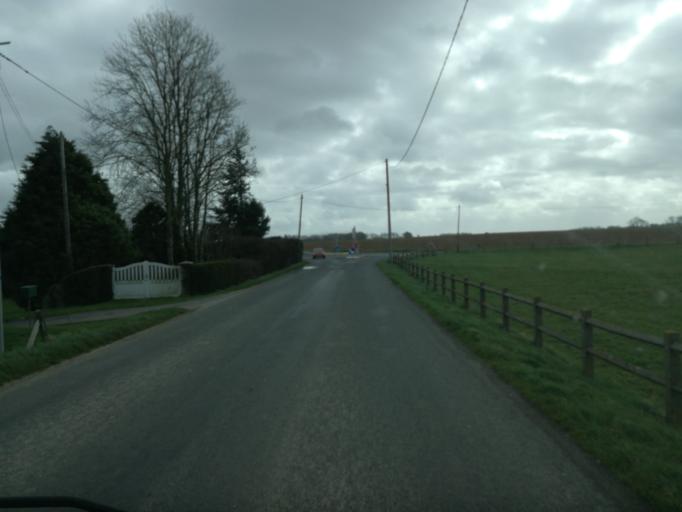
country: FR
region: Haute-Normandie
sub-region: Departement de la Seine-Maritime
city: Yebleron
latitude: 49.6612
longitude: 0.5112
